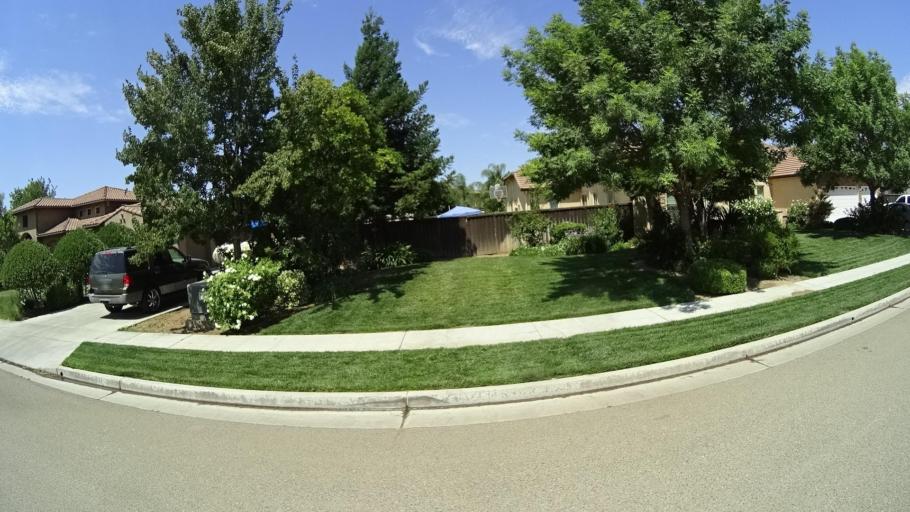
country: US
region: California
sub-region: Fresno County
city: Sunnyside
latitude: 36.7266
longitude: -119.7111
